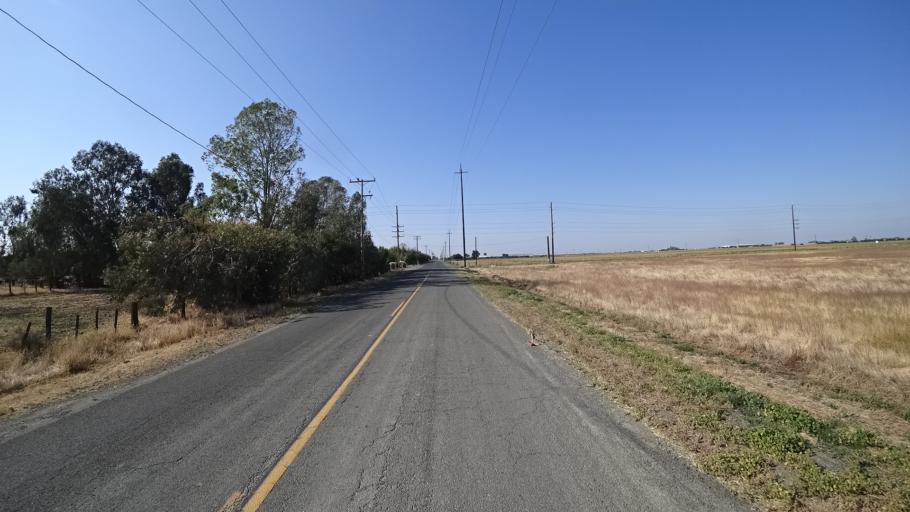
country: US
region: California
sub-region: Kings County
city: Home Garden
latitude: 36.3145
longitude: -119.5831
